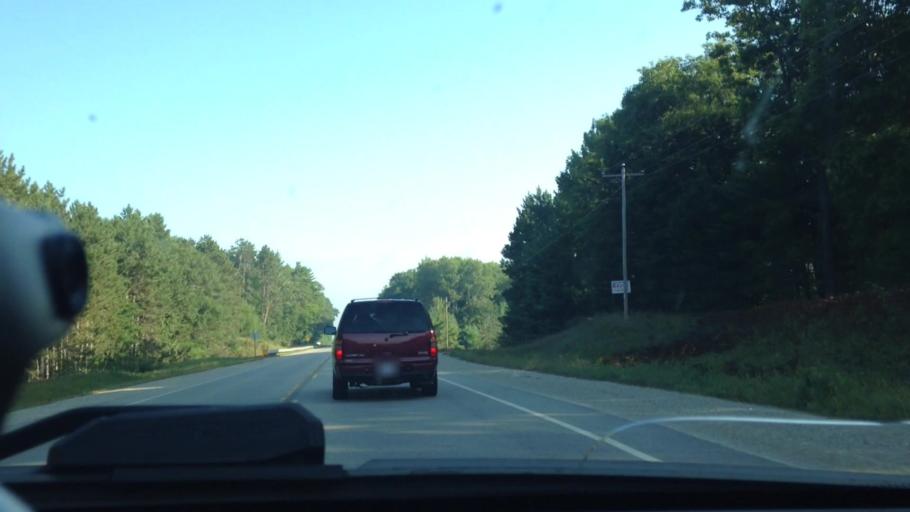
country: US
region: Wisconsin
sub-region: Marinette County
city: Peshtigo
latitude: 45.1675
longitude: -87.9963
